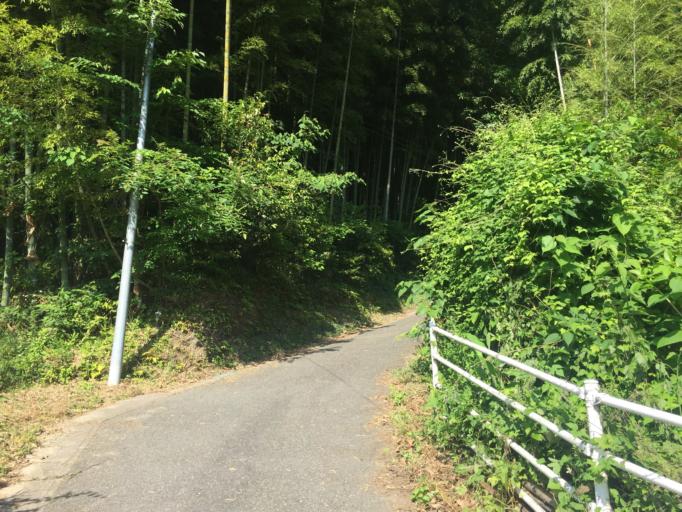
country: JP
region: Hiroshima
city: Takehara
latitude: 34.4459
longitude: 132.7856
